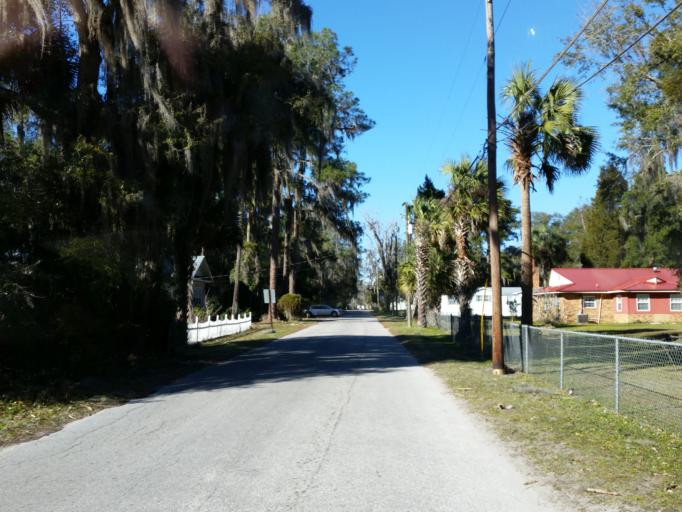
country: US
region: Florida
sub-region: Hamilton County
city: Jasper
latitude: 30.5138
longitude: -82.9514
